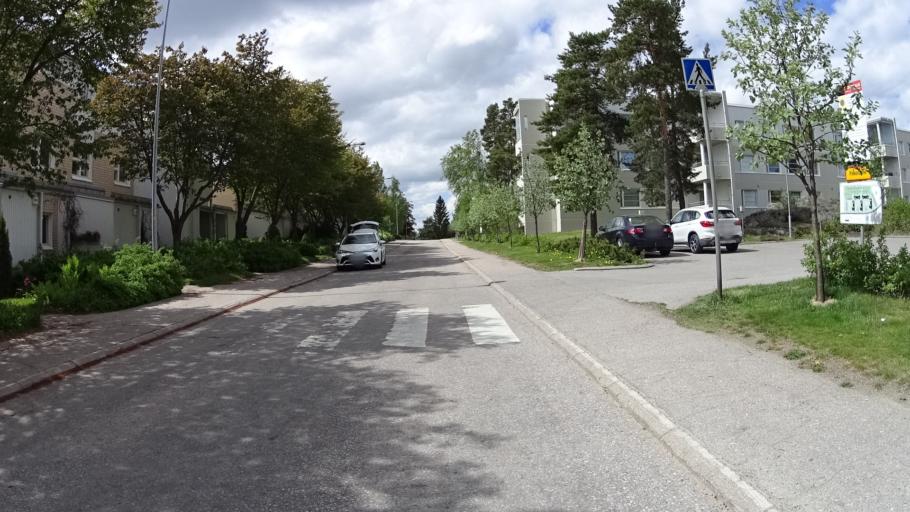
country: FI
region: Uusimaa
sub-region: Helsinki
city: Otaniemi
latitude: 60.1670
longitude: 24.7977
